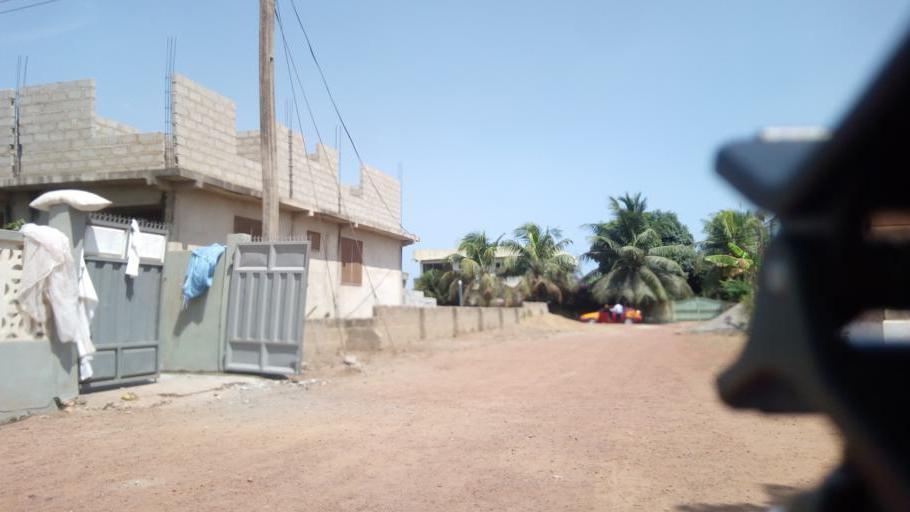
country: GH
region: Central
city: Cape Coast
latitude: 5.1318
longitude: -1.2797
